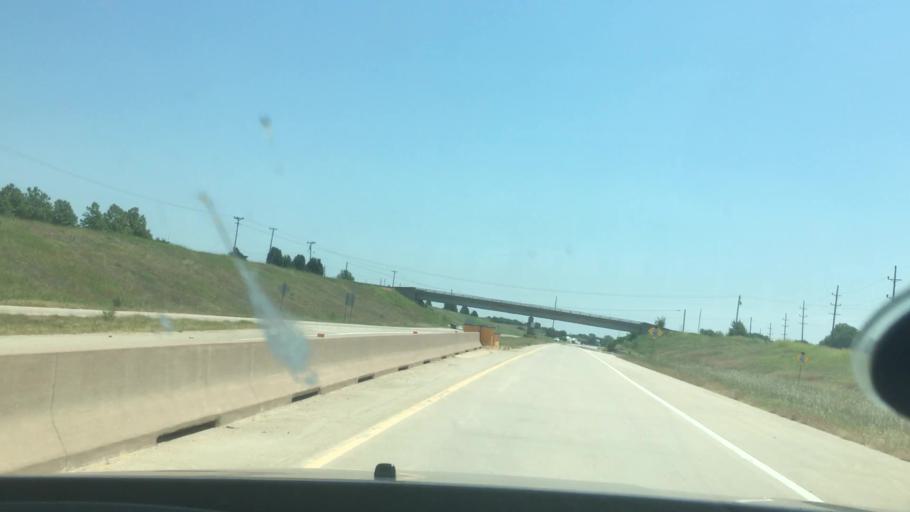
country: US
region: Oklahoma
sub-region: Pontotoc County
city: Ada
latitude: 34.7894
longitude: -96.6897
